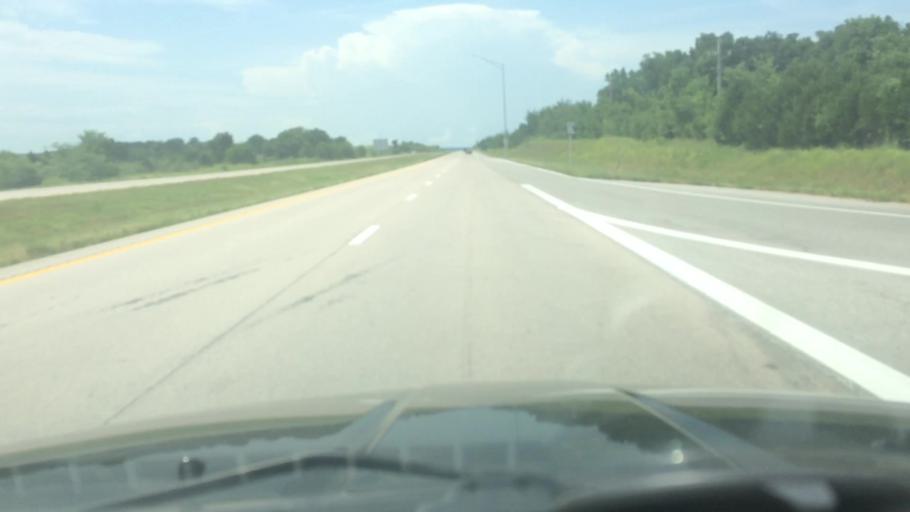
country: US
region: Missouri
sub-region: Polk County
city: Humansville
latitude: 37.7955
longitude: -93.5897
